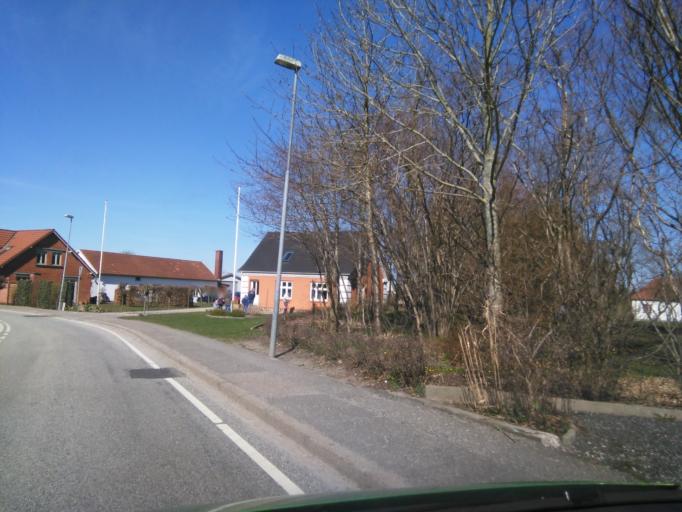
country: DK
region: Central Jutland
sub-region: Horsens Kommune
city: Braedstrup
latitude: 56.0219
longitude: 9.6418
